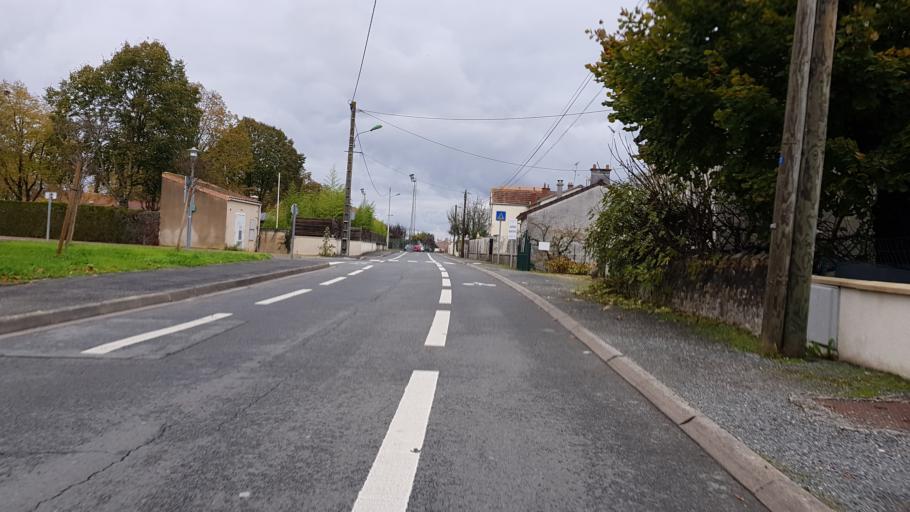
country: FR
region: Poitou-Charentes
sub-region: Departement de la Vienne
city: Chasseneuil-du-Poitou
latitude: 46.6541
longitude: 0.3778
